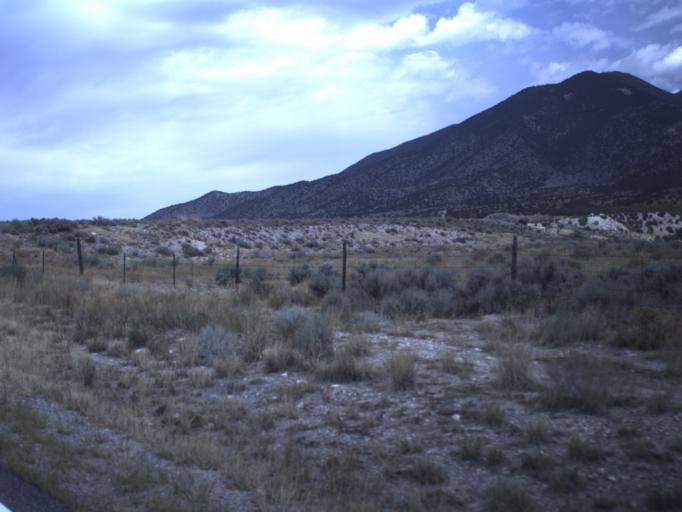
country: US
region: Utah
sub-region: Tooele County
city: Tooele
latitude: 40.3469
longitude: -112.3073
